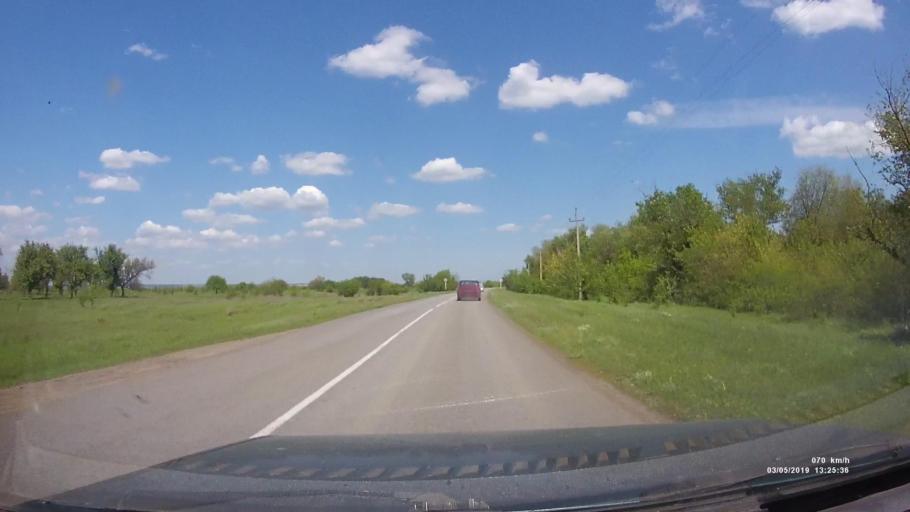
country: RU
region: Rostov
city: Semikarakorsk
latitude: 47.5675
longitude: 40.8060
